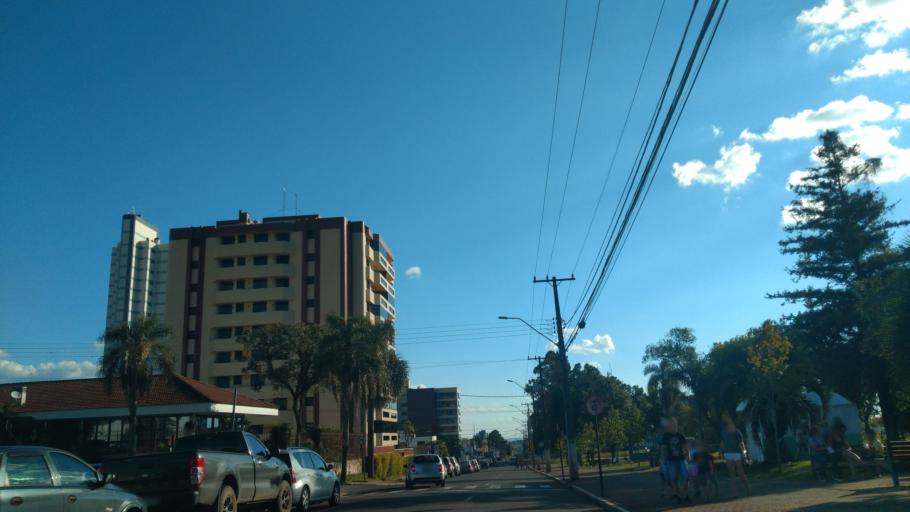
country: BR
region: Parana
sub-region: Guarapuava
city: Guarapuava
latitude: -25.3954
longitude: -51.4612
